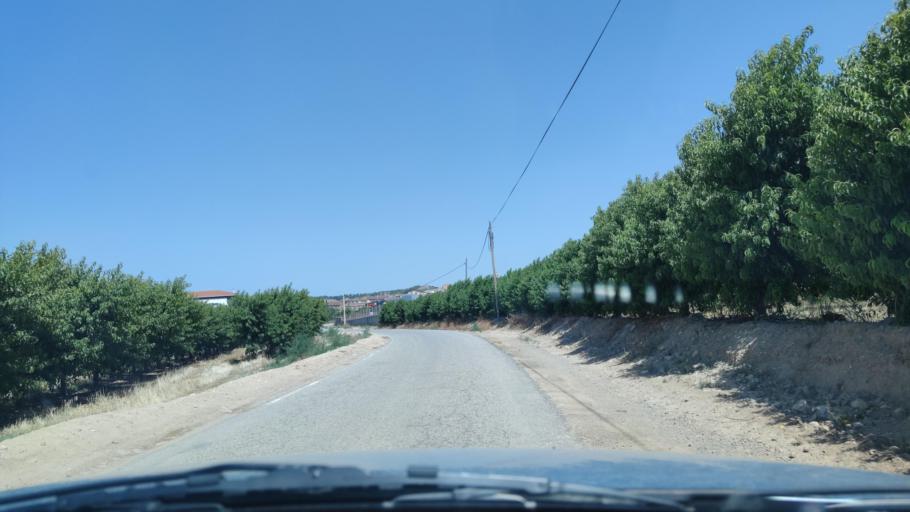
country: ES
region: Catalonia
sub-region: Provincia de Lleida
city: Alpicat
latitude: 41.6609
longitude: 0.5606
